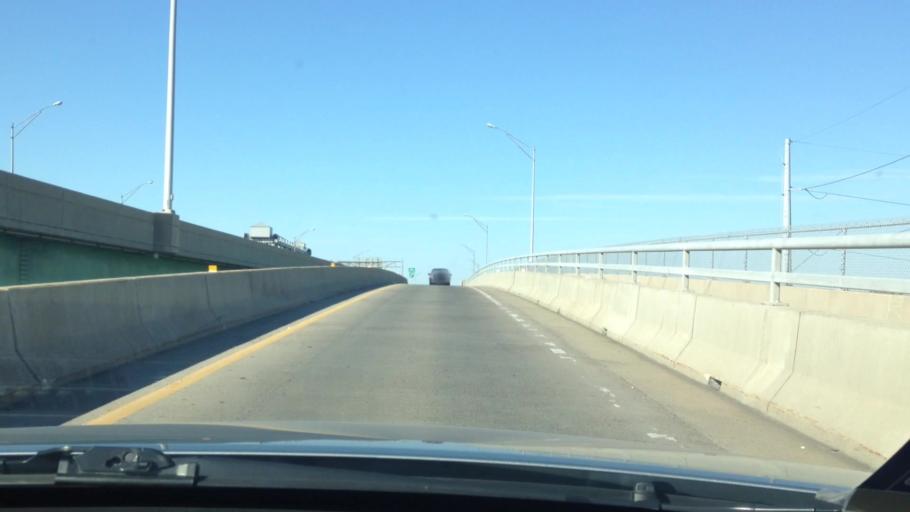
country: US
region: Missouri
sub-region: Jackson County
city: Kansas City
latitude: 39.1122
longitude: -94.5777
